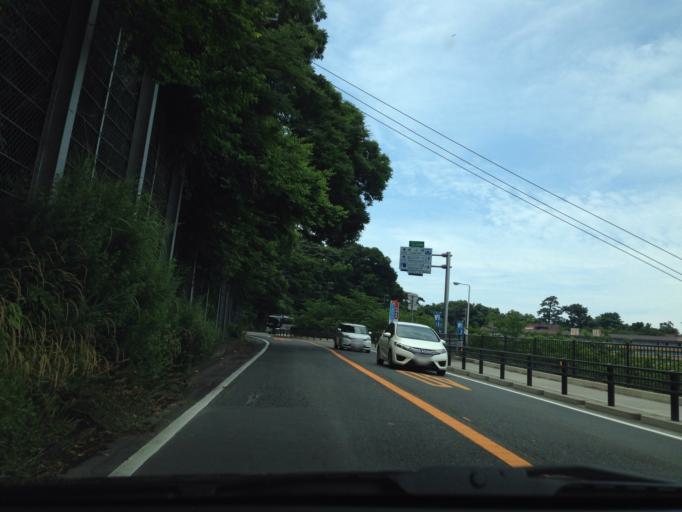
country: JP
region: Shizuoka
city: Heda
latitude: 34.9053
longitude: 138.7856
